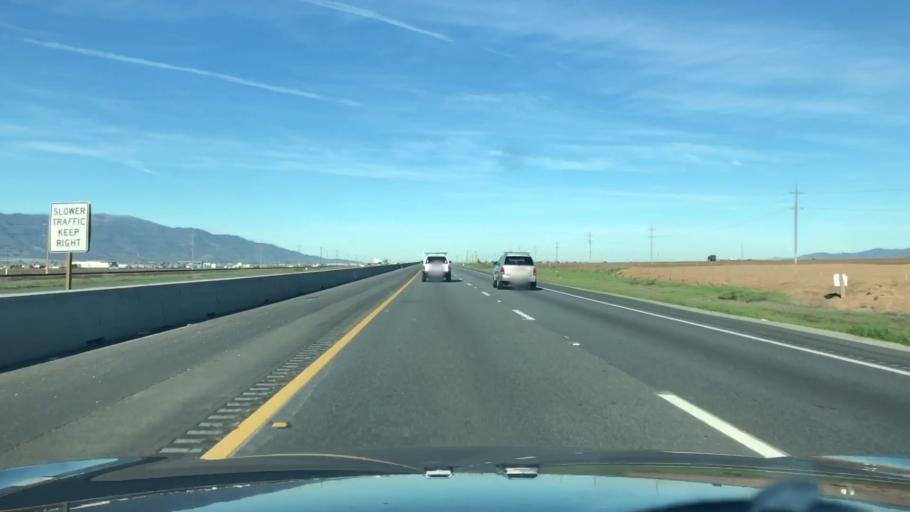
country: US
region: California
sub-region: Monterey County
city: Gonzales
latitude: 36.4716
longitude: -121.3986
